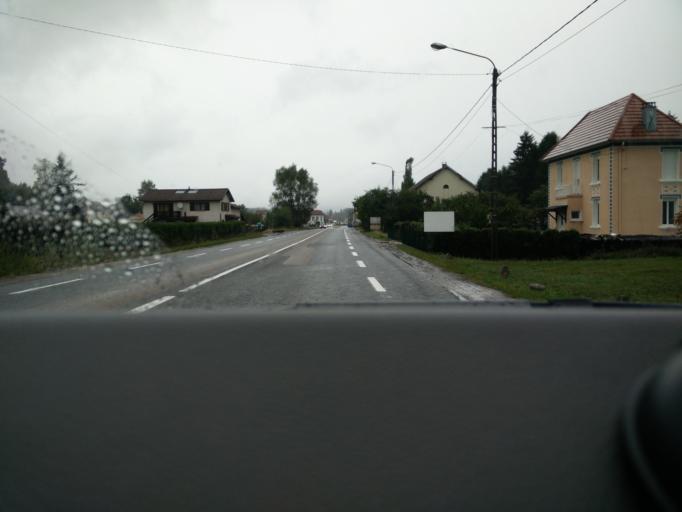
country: FR
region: Lorraine
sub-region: Departement des Vosges
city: Saulcy-sur-Meurthe
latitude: 48.2345
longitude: 6.9507
